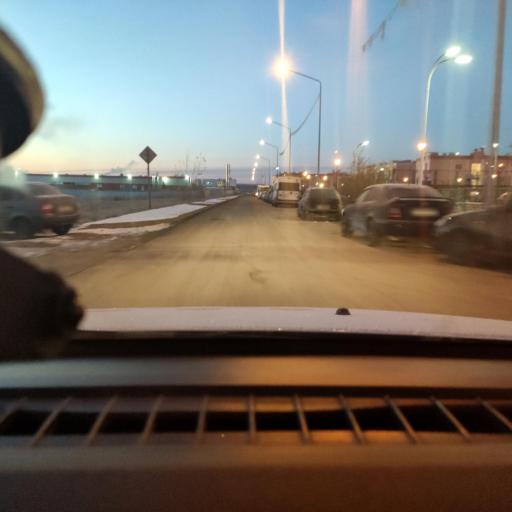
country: RU
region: Samara
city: Samara
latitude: 53.1169
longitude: 50.1632
